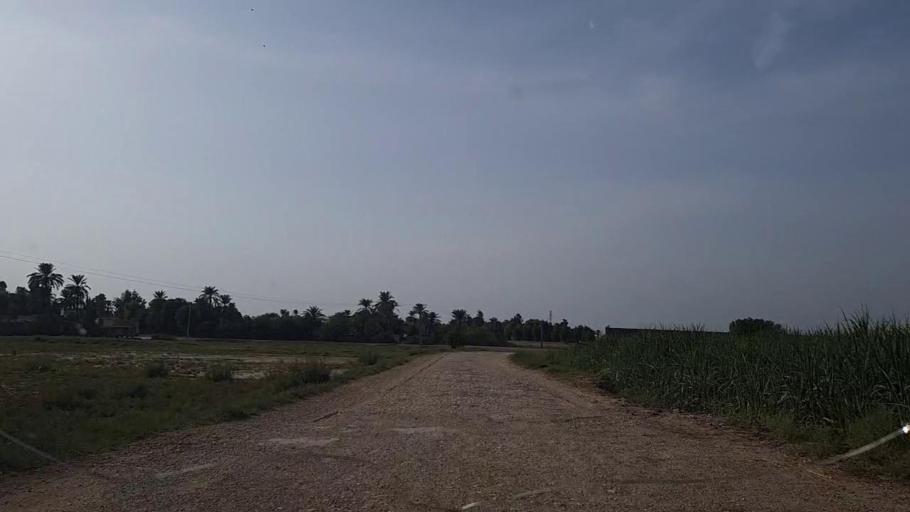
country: PK
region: Sindh
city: Ghotki
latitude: 28.0077
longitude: 69.2959
